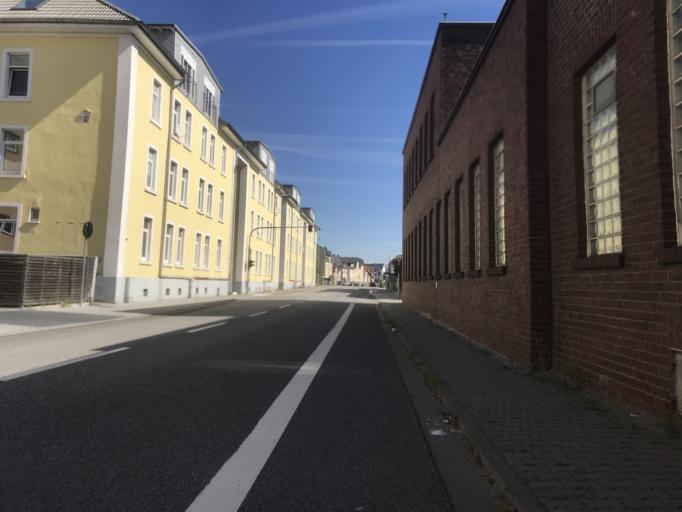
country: DE
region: Hesse
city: Kelsterbach
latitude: 50.0589
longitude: 8.5194
